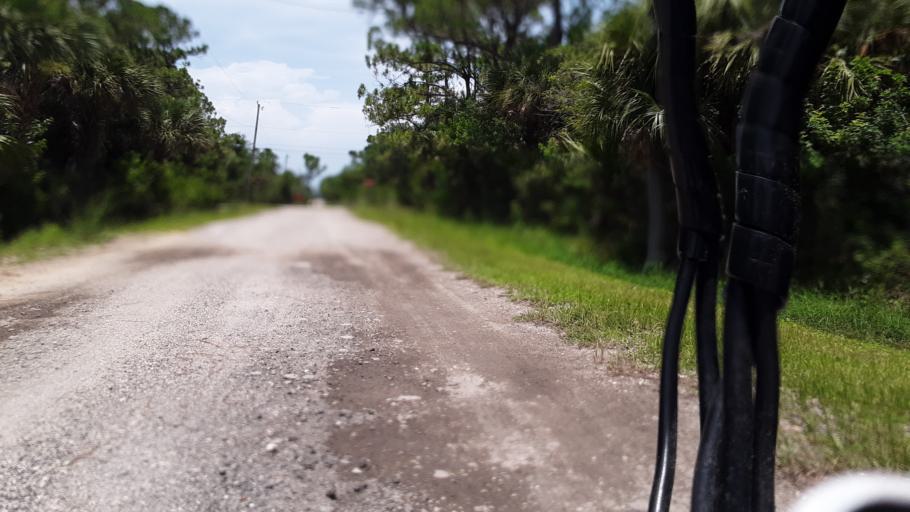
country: US
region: Florida
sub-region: Brevard County
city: Malabar
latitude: 27.9828
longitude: -80.5978
